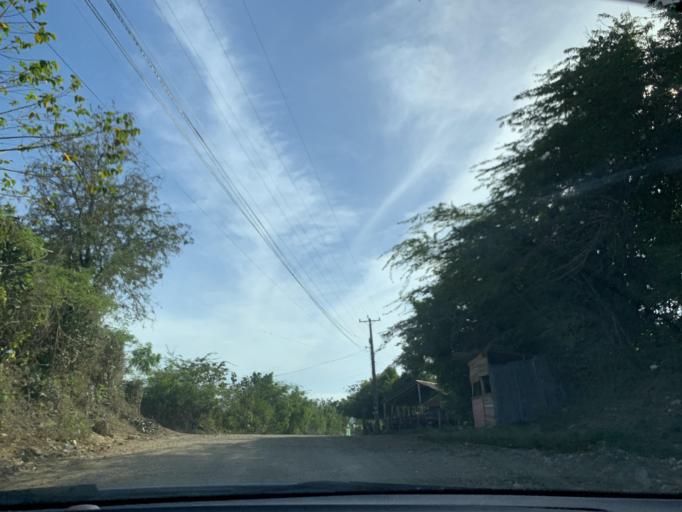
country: DO
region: Puerto Plata
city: Luperon
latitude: 19.8755
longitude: -70.9355
